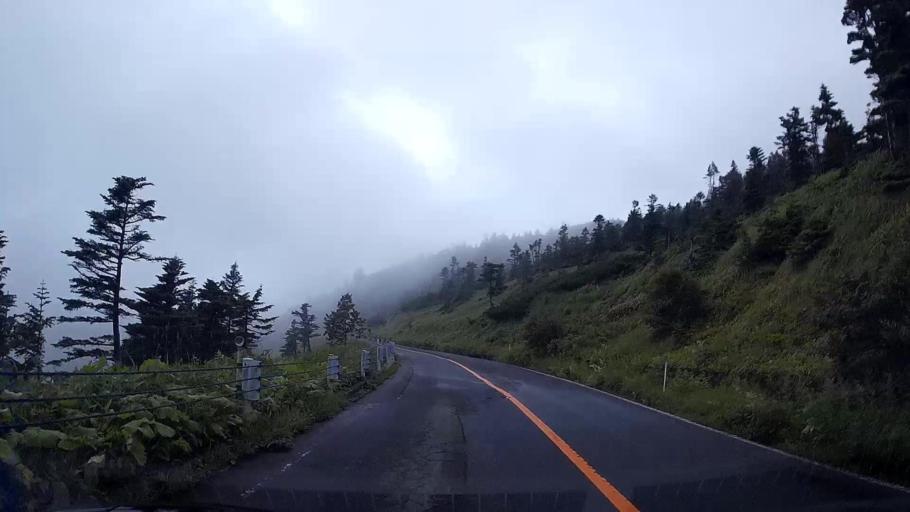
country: JP
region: Nagano
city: Nakano
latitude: 36.6585
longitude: 138.5323
